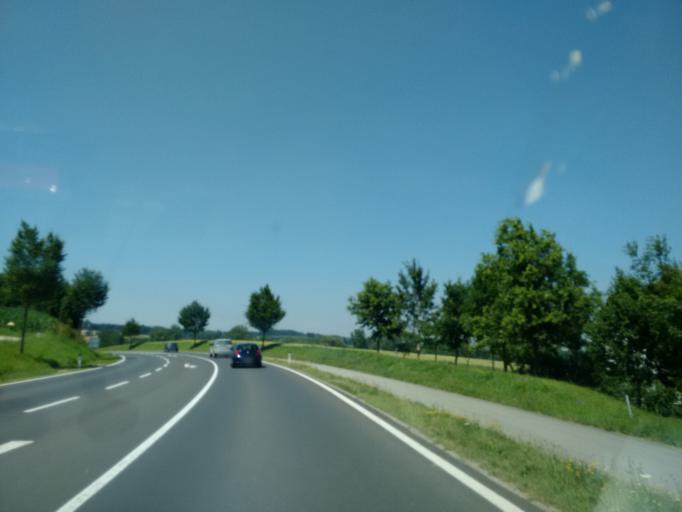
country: AT
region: Upper Austria
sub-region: Politischer Bezirk Grieskirchen
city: Bad Schallerbach
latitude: 48.2322
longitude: 13.9664
